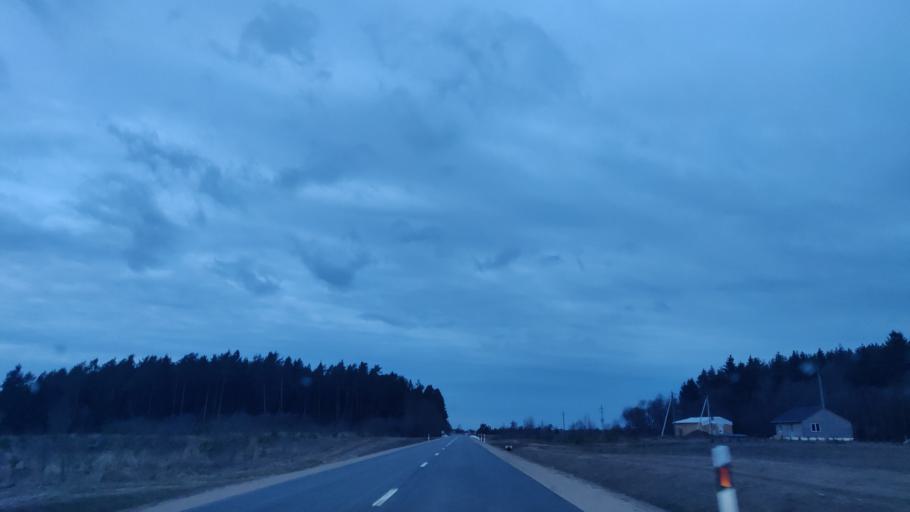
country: LT
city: Lentvaris
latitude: 54.5976
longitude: 25.0290
